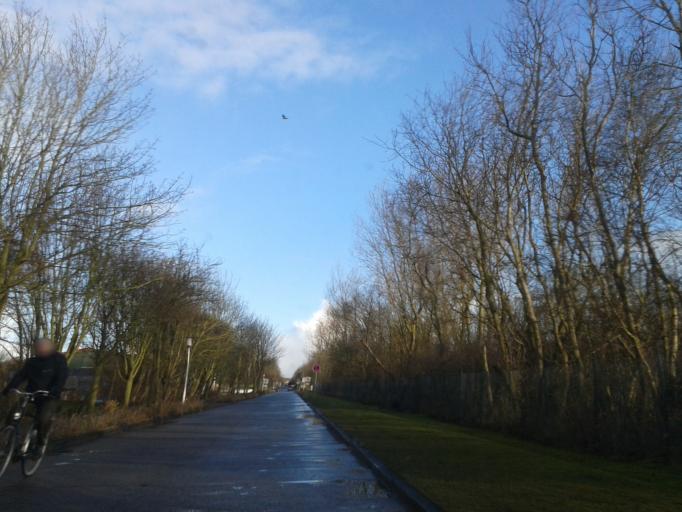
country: DE
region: Lower Saxony
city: Norderney
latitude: 53.7034
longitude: 7.1567
